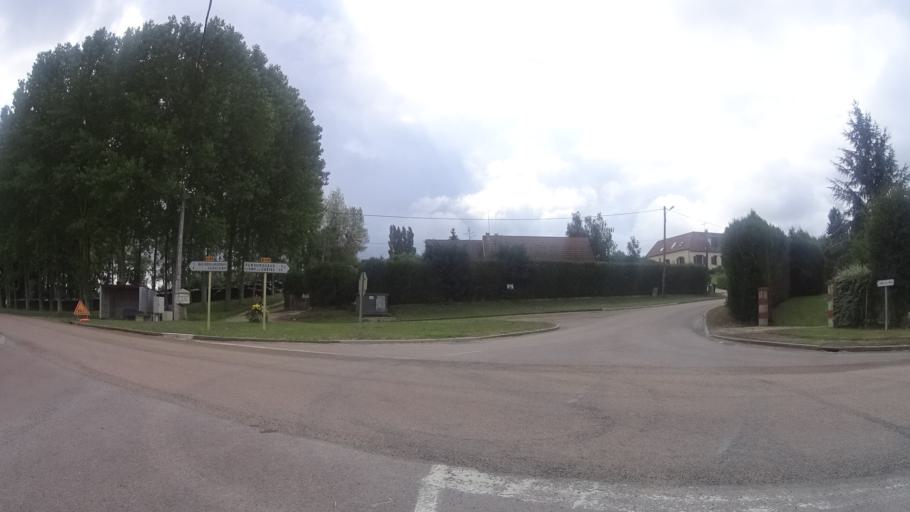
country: FR
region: Bourgogne
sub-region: Departement de l'Yonne
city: Vergigny
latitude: 47.9639
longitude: 3.6701
